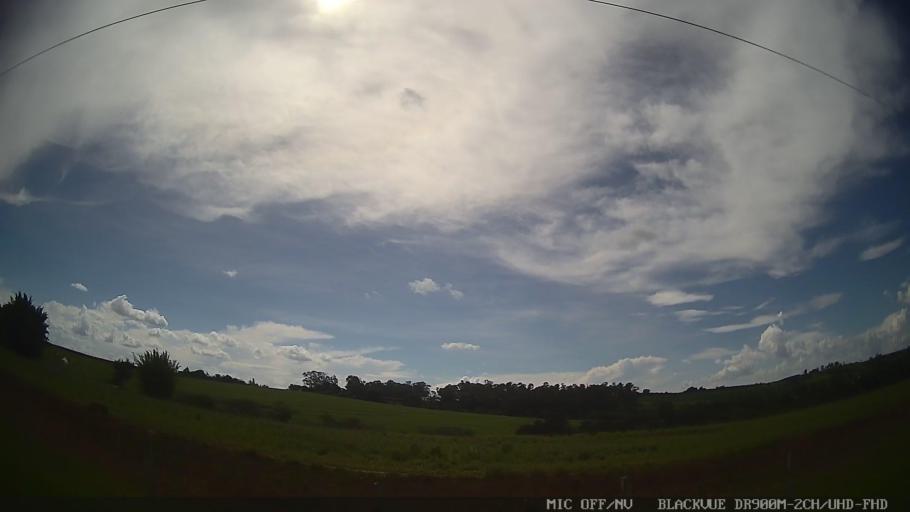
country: BR
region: Sao Paulo
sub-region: Conchas
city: Conchas
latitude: -22.9670
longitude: -47.9838
